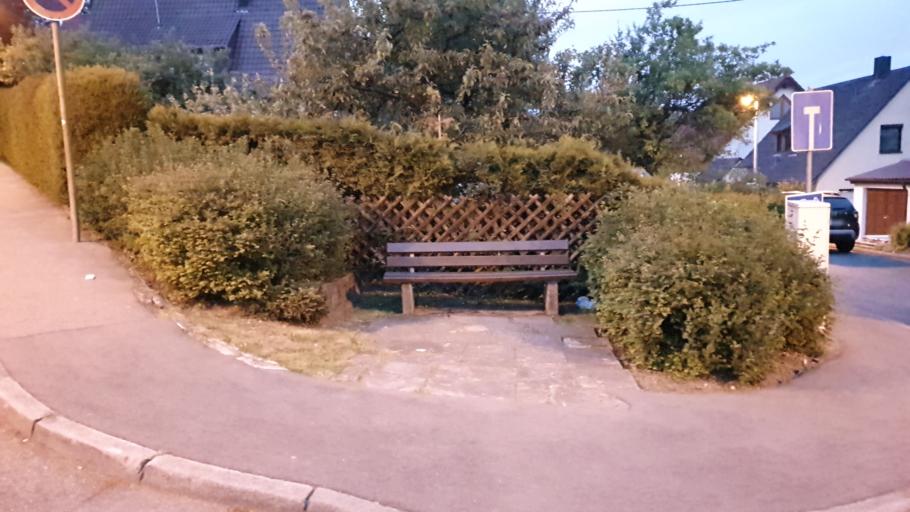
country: DE
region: Baden-Wuerttemberg
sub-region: Regierungsbezirk Stuttgart
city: Leonberg
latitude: 48.7998
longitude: 8.9998
